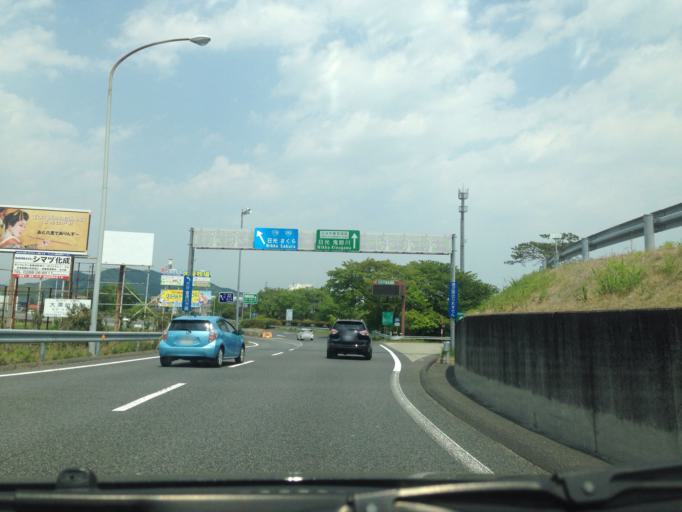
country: JP
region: Tochigi
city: Utsunomiya-shi
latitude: 36.6355
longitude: 139.8451
